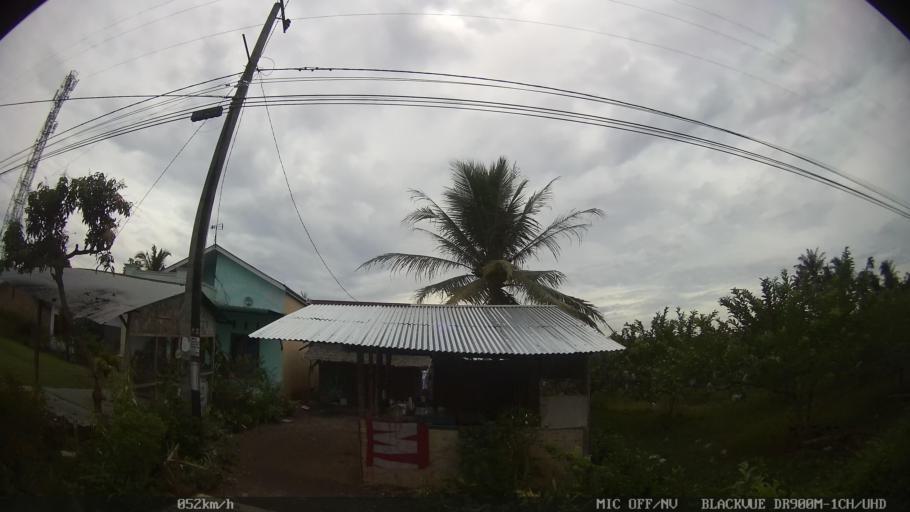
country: ID
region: North Sumatra
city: Sunggal
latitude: 3.5741
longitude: 98.5646
